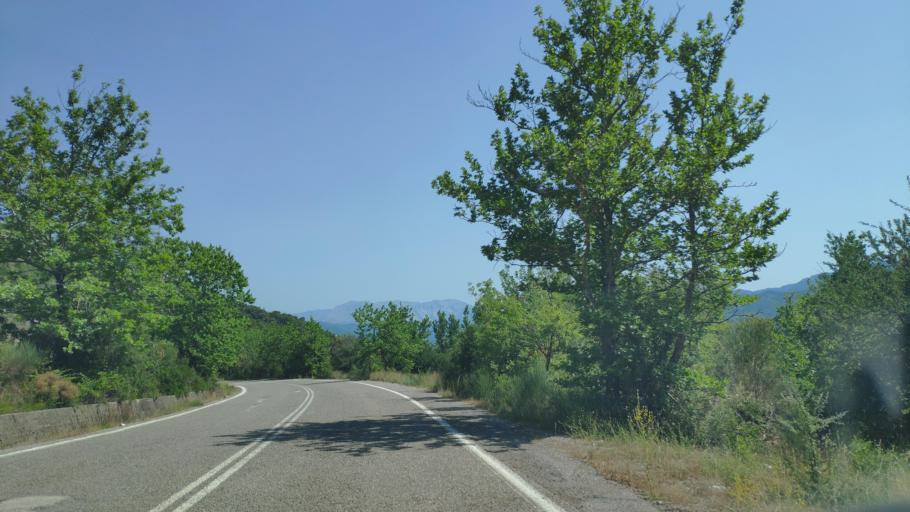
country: GR
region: West Greece
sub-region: Nomos Aitolias kai Akarnanias
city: Lepenou
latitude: 38.8036
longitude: 21.3331
